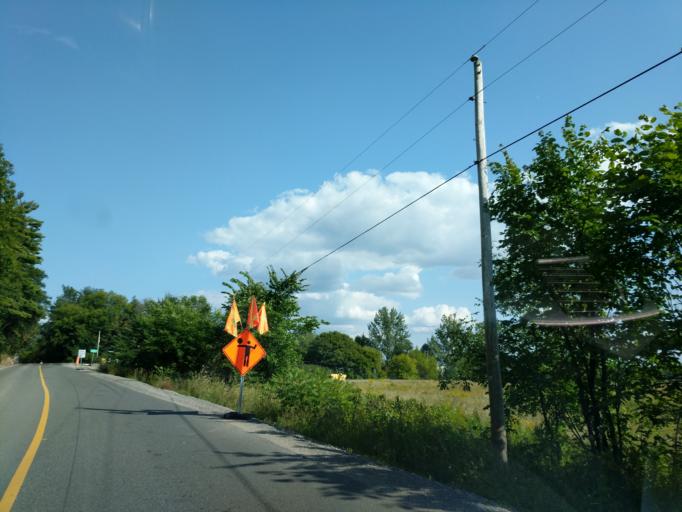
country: CA
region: Quebec
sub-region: Outaouais
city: Wakefield
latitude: 45.4954
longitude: -75.9116
